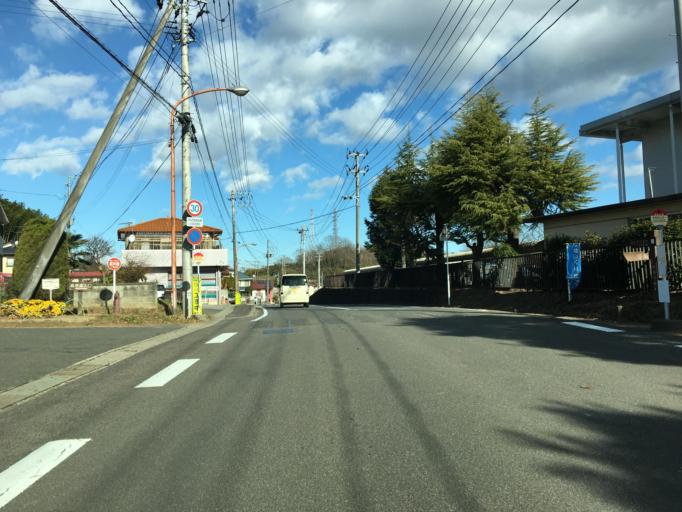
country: JP
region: Fukushima
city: Nihommatsu
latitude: 37.5939
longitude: 140.4503
